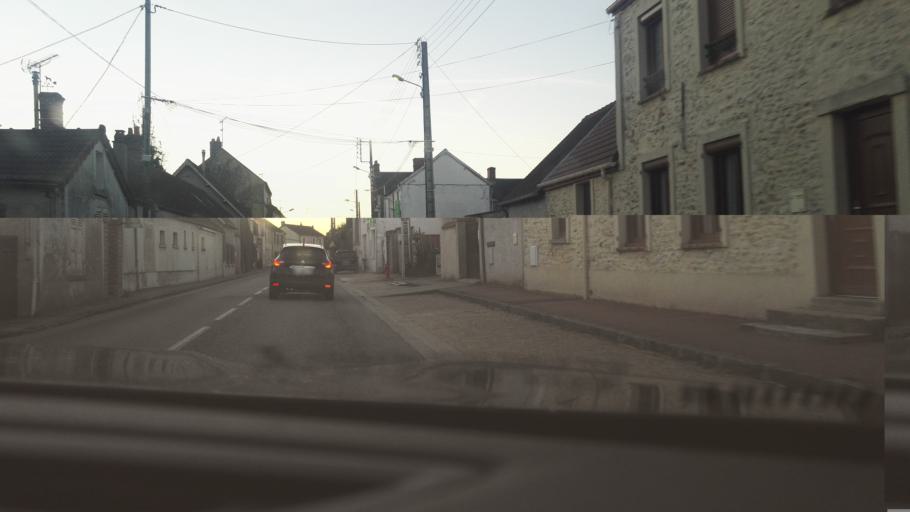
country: FR
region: Ile-de-France
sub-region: Departement des Yvelines
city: Longnes
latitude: 48.9196
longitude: 1.5865
